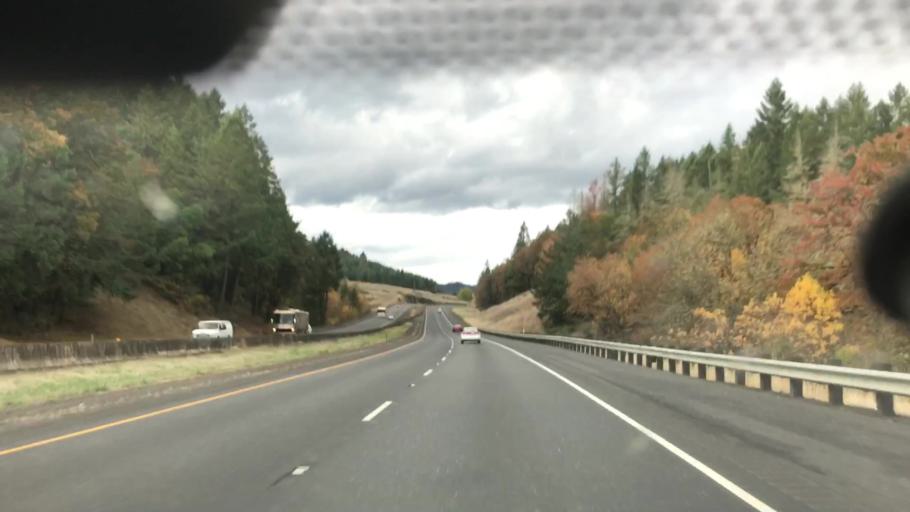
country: US
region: Oregon
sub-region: Douglas County
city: Sutherlin
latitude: 43.4852
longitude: -123.3258
